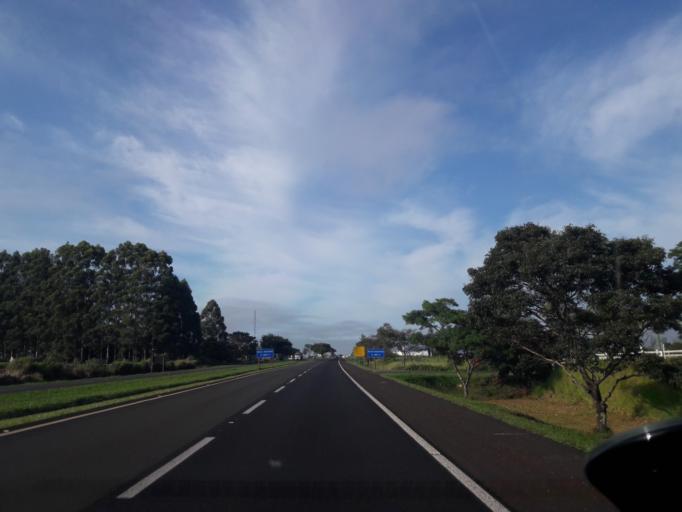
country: BR
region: Parana
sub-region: Rolandia
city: Rolandia
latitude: -23.3441
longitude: -51.3757
